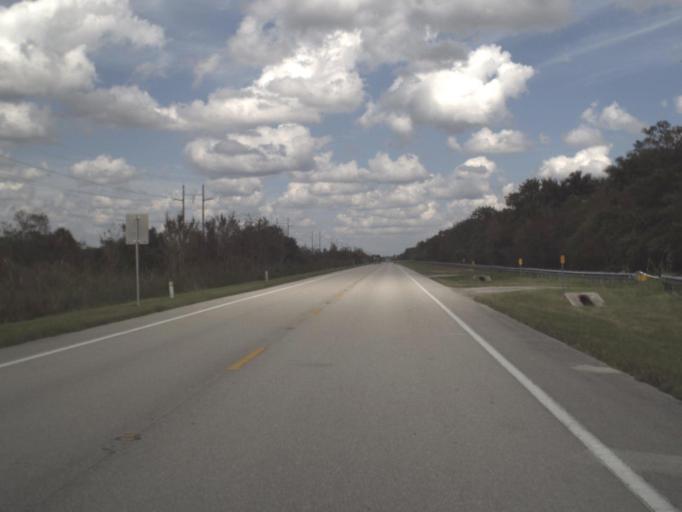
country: US
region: Florida
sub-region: Collier County
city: Lely Resort
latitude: 25.9576
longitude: -81.3555
